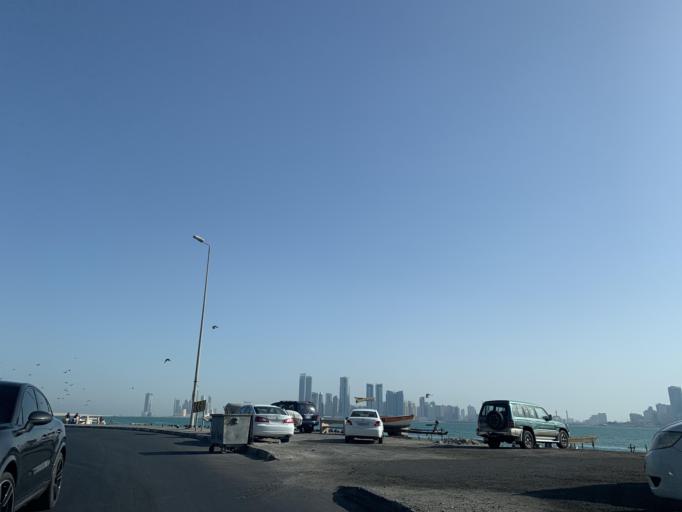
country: BH
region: Muharraq
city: Al Muharraq
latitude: 26.2448
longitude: 50.6090
